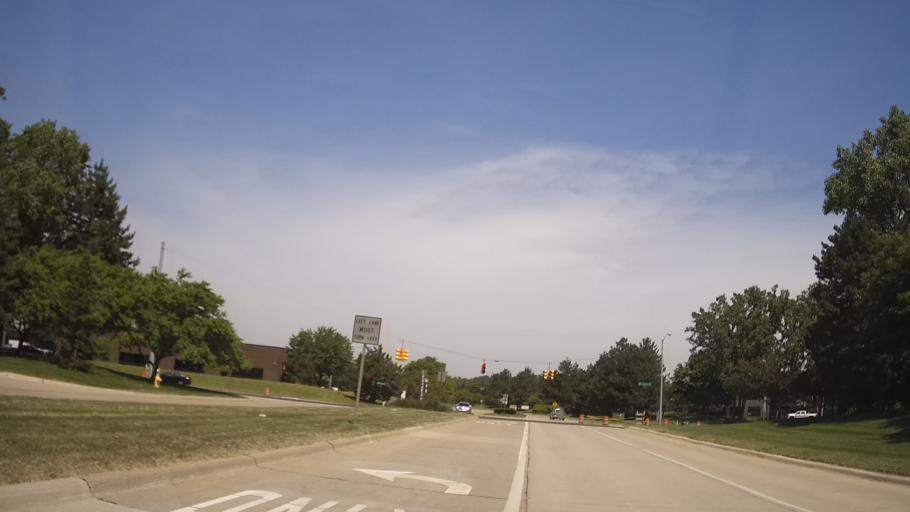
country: US
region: Michigan
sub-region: Wayne County
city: Dearborn
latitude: 42.3071
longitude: -83.1821
